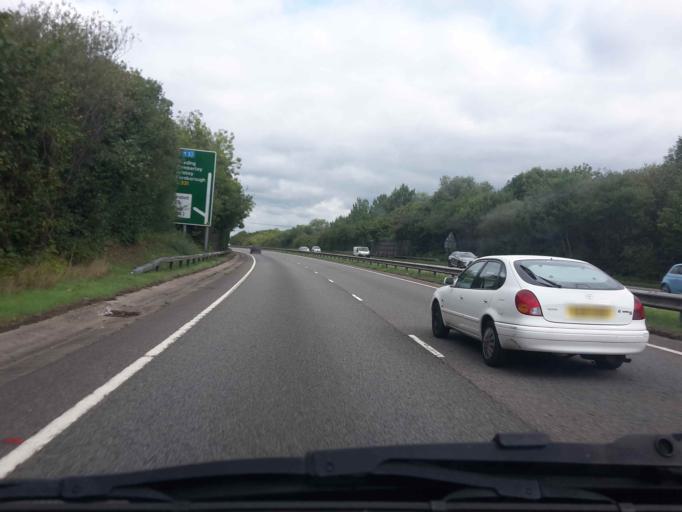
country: GB
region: England
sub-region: Surrey
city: Seale
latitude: 51.2362
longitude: -0.7353
